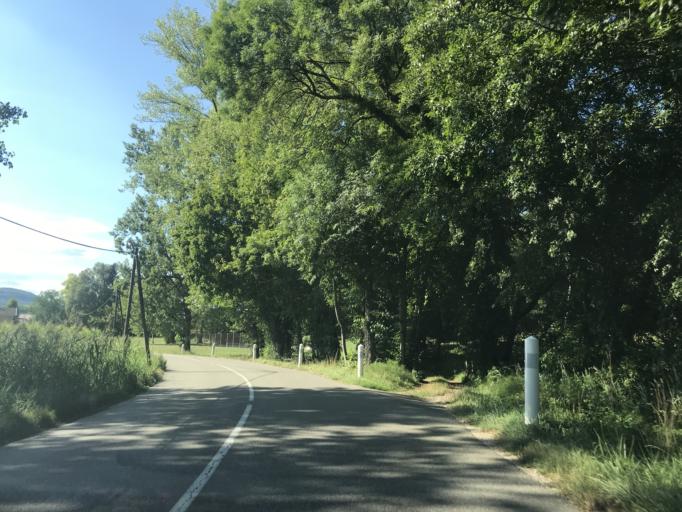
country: FR
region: Rhone-Alpes
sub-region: Departement de la Savoie
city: Yenne
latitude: 45.7492
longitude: 5.7909
